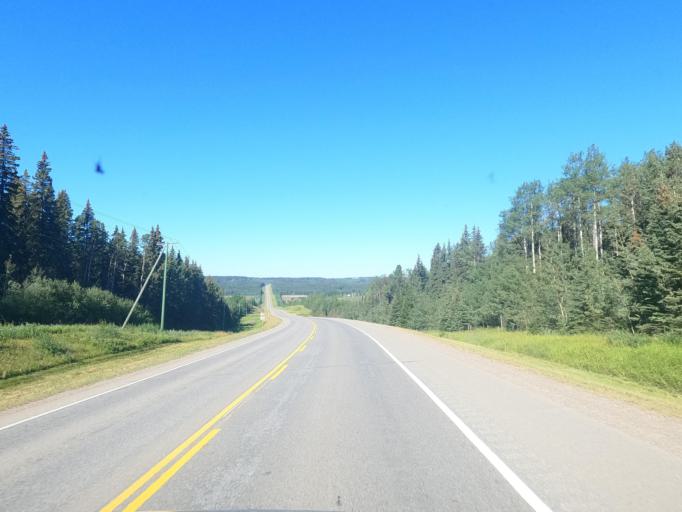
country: CA
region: British Columbia
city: Fort St. John
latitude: 56.6299
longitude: -121.5197
